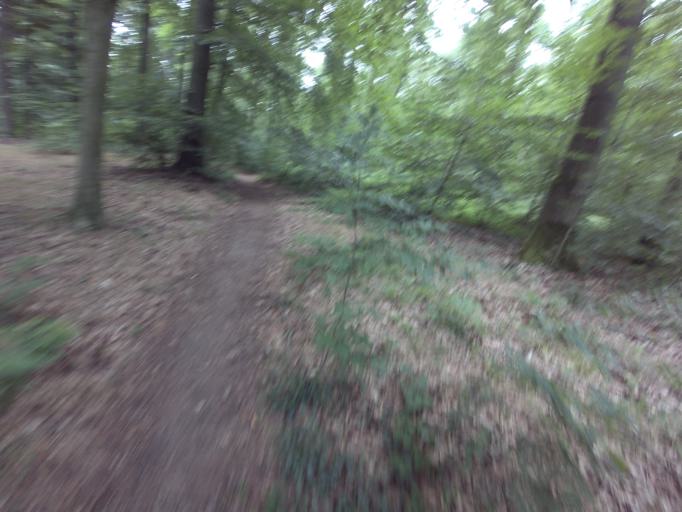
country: BE
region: Wallonia
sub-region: Province de Liege
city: La Calamine
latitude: 50.7008
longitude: 6.0199
